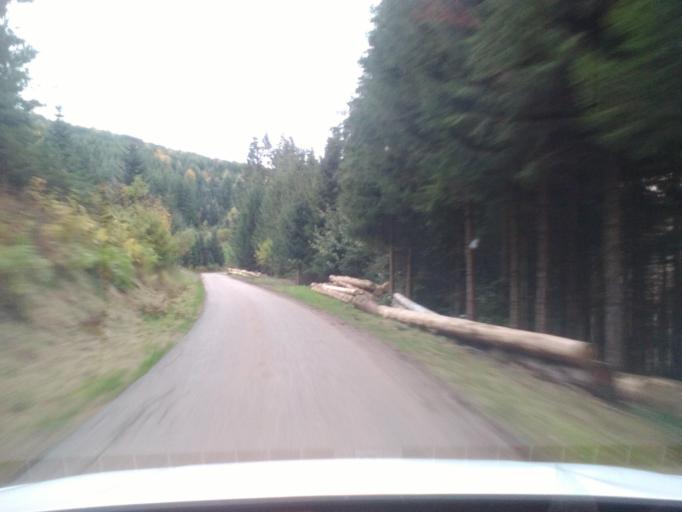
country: FR
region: Lorraine
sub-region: Departement des Vosges
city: Senones
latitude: 48.3774
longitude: 7.0835
